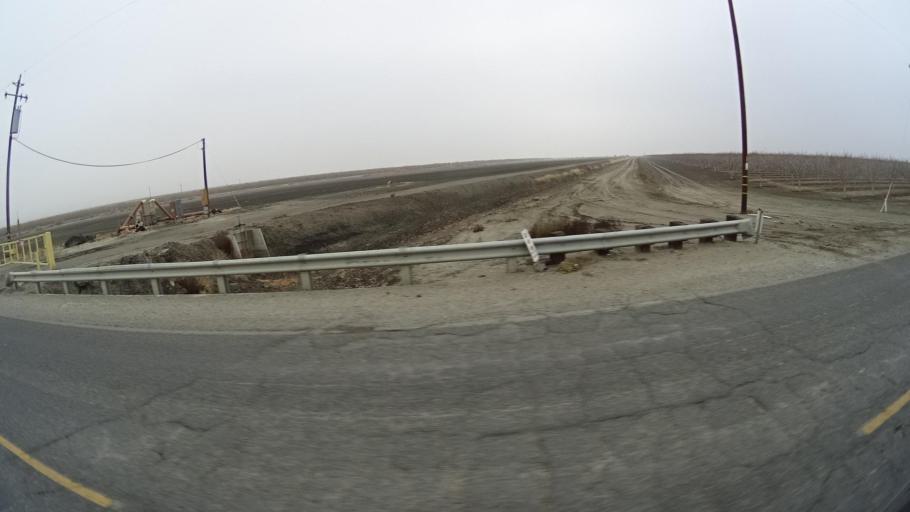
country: US
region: California
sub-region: Kern County
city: Buttonwillow
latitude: 35.3633
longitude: -119.4742
